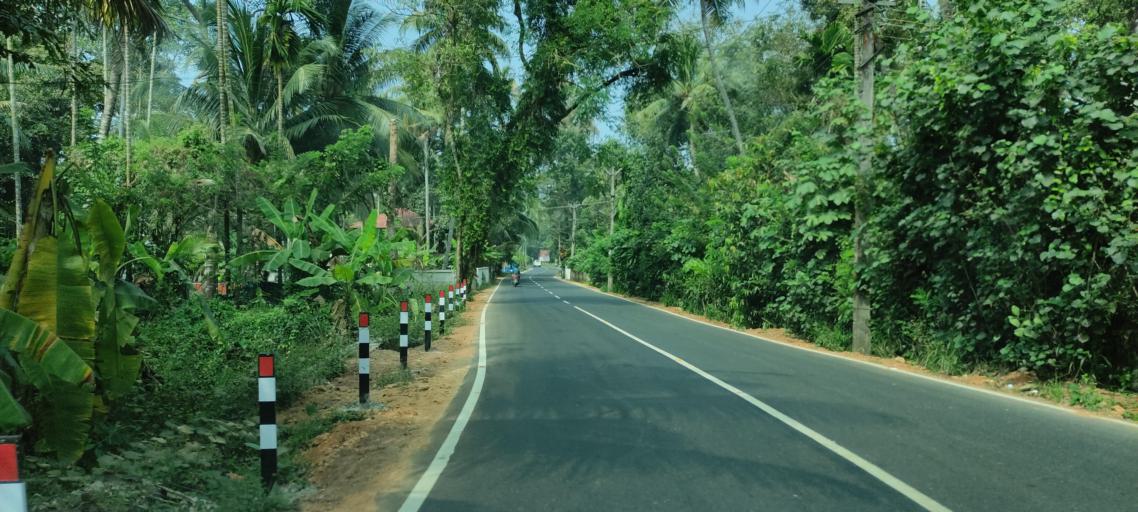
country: IN
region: Kerala
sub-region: Alappuzha
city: Shertallai
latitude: 9.6679
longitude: 76.3883
